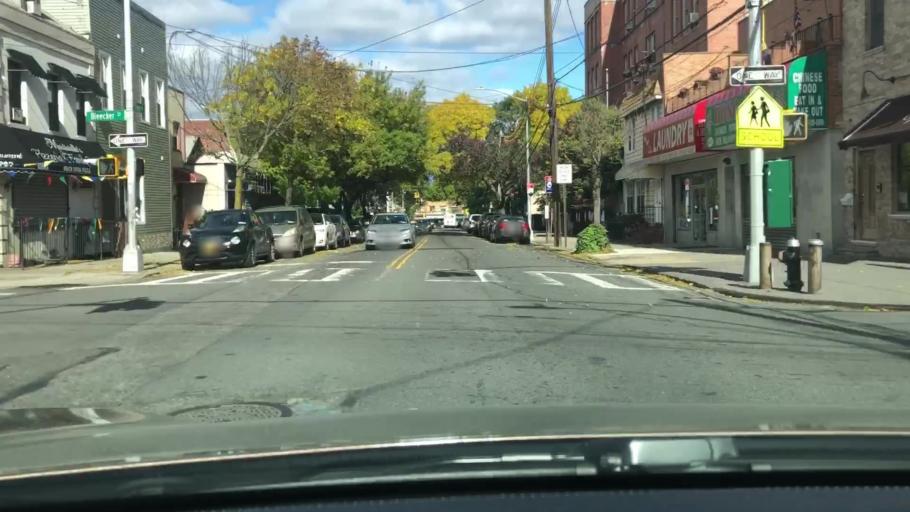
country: US
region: New York
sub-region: Kings County
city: East New York
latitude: 40.7108
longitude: -73.9051
